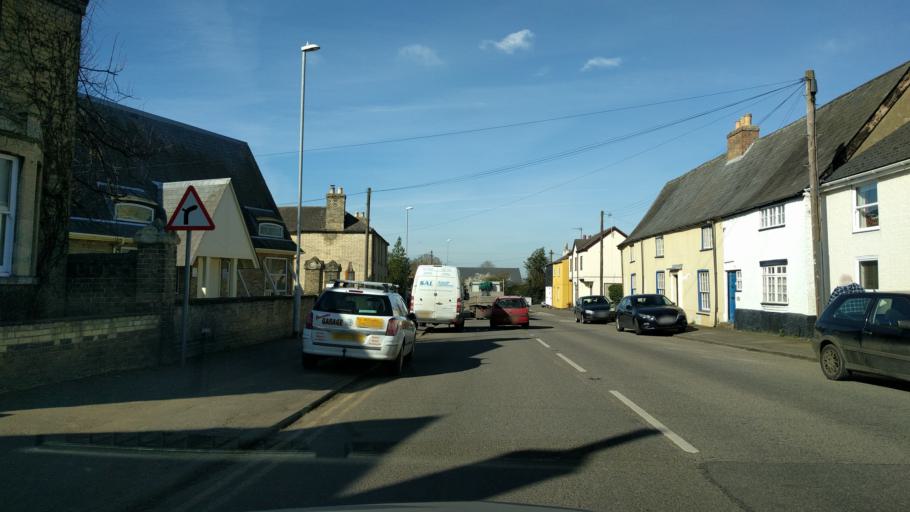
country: GB
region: England
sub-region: Cambridgeshire
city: Earith
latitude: 52.3145
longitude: 0.0579
